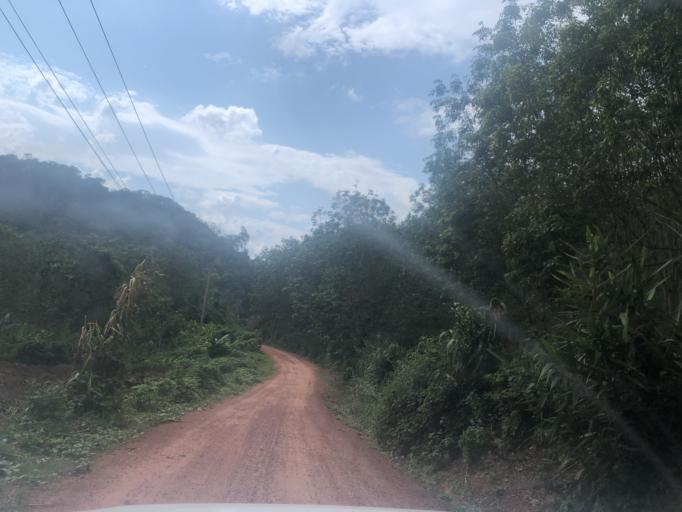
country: LA
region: Oudomxai
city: Muang La
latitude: 21.2436
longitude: 101.9362
